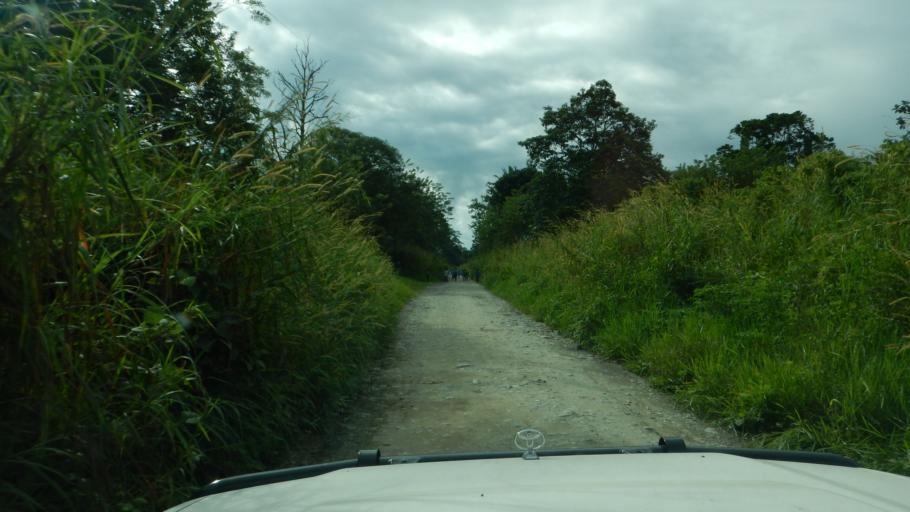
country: PG
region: Northern Province
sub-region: Sohe
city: Kokoda
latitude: -8.8896
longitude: 147.7474
